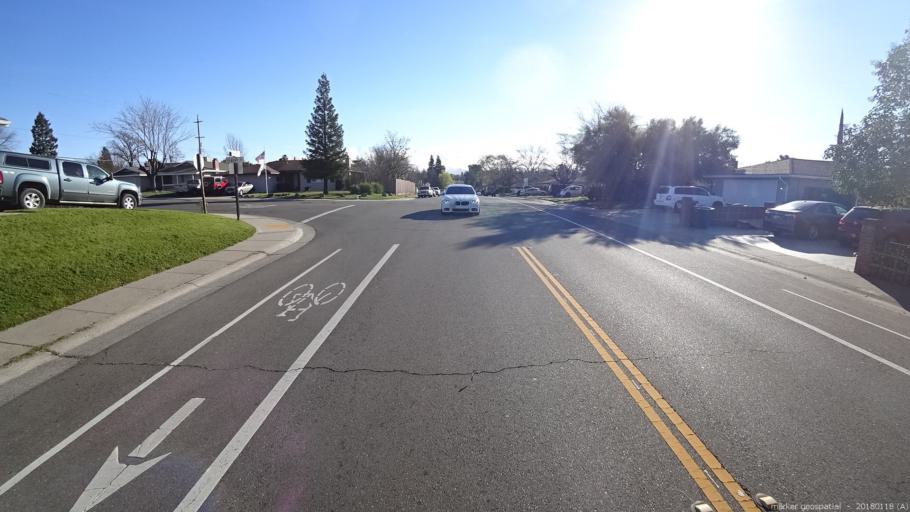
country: US
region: California
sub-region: Sacramento County
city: Orangevale
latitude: 38.6706
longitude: -121.2167
